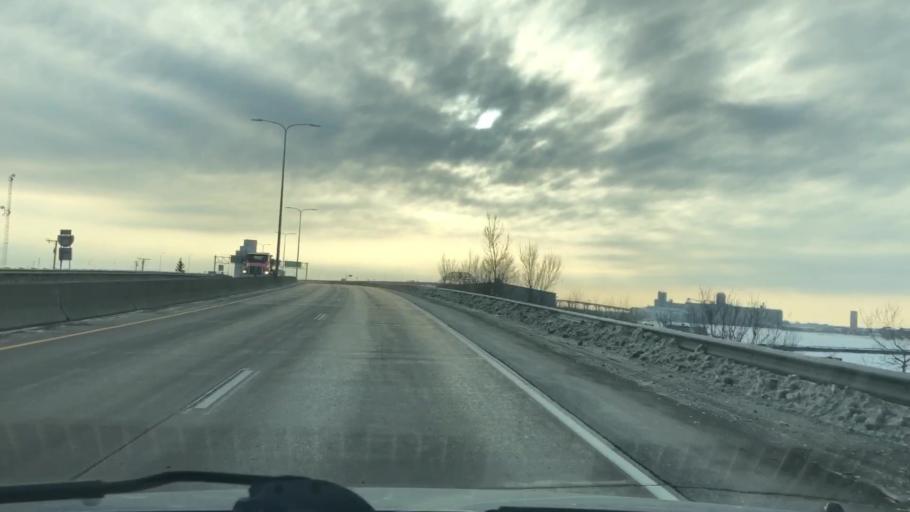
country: US
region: Minnesota
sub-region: Saint Louis County
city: Duluth
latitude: 46.7595
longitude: -92.1130
